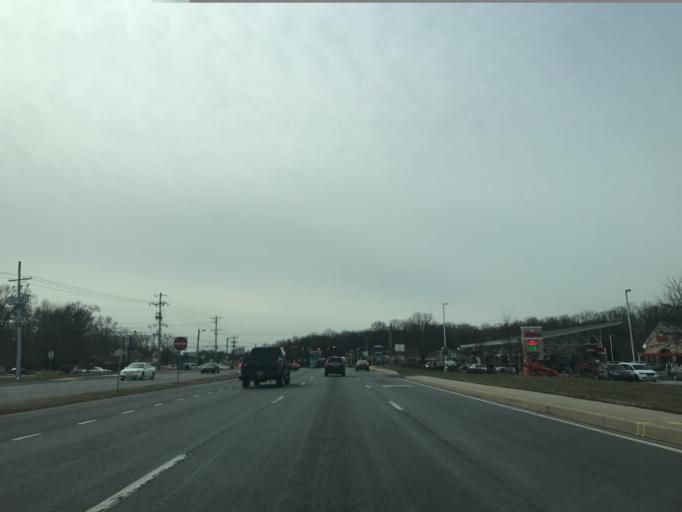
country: US
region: Delaware
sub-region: New Castle County
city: Bear
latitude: 39.6195
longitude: -75.6930
